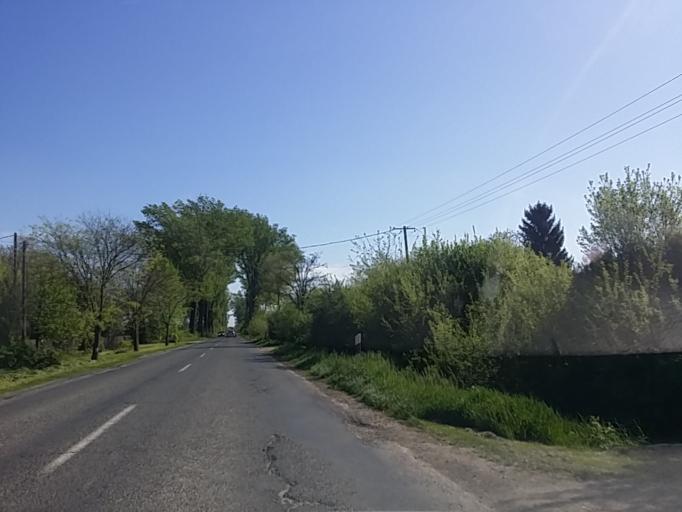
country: HU
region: Bekes
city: Bekes
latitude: 46.7104
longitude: 21.1787
